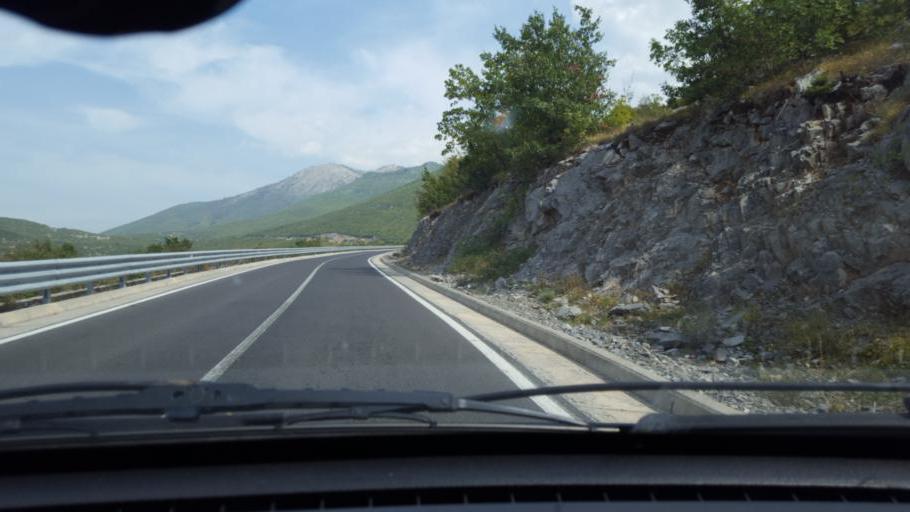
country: AL
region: Shkoder
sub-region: Rrethi i Malesia e Madhe
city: Kastrat
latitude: 42.3707
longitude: 19.4722
